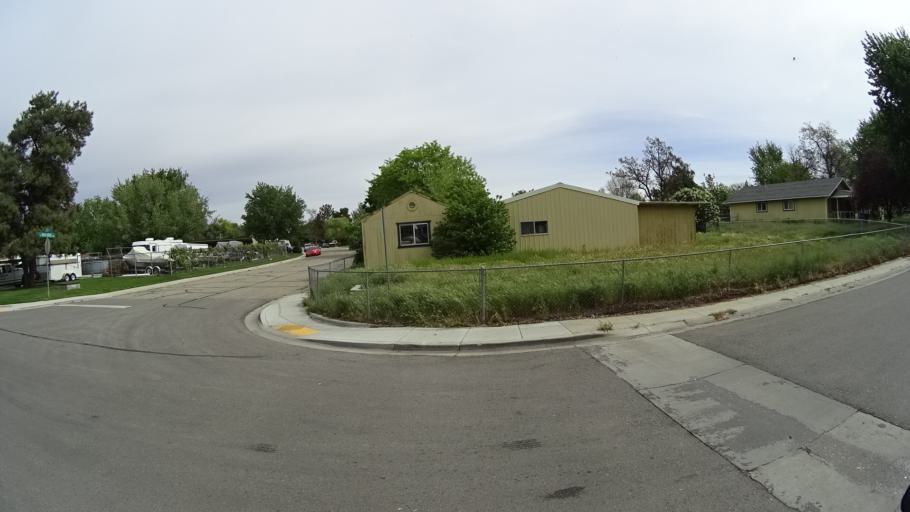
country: US
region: Idaho
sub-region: Ada County
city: Garden City
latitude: 43.5348
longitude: -116.3072
